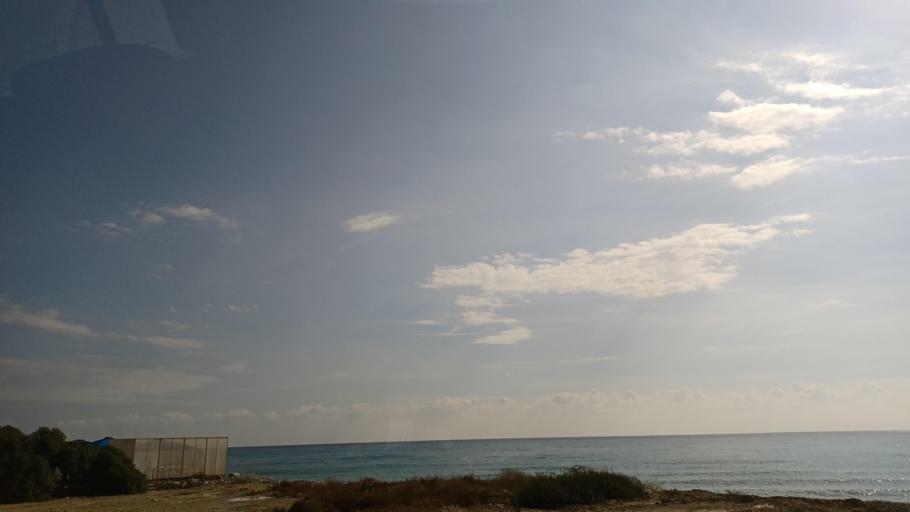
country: CY
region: Larnaka
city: Kofinou
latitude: 34.7505
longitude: 33.4084
